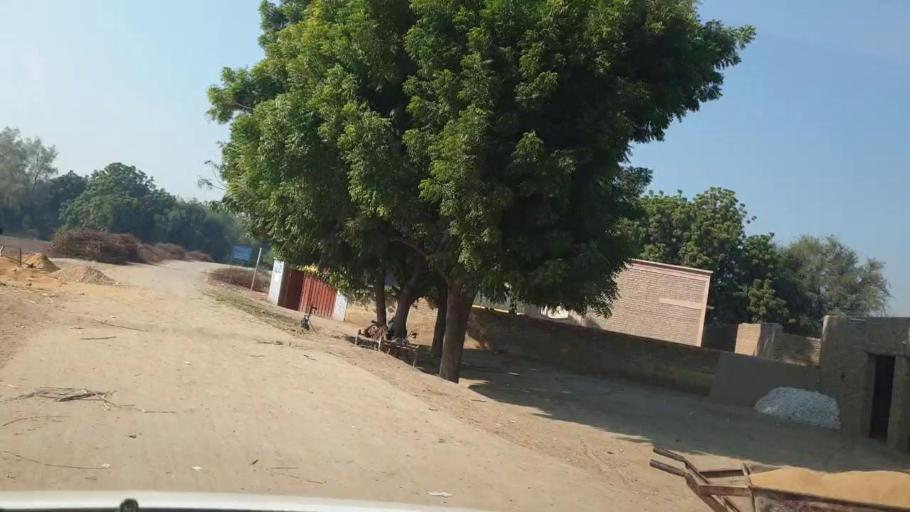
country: PK
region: Sindh
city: Bhan
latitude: 26.6040
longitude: 67.7477
